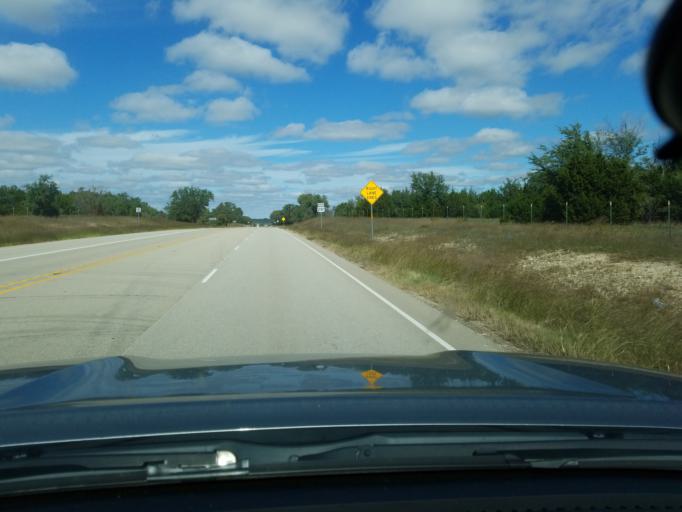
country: US
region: Texas
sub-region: Hamilton County
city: Hamilton
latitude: 31.5930
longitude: -98.1570
